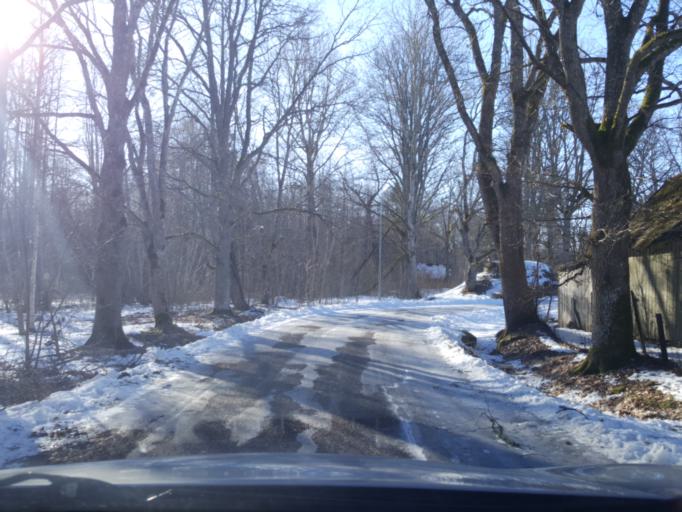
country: EE
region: Viljandimaa
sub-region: Suure-Jaani vald
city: Suure-Jaani
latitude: 58.5457
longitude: 25.5477
